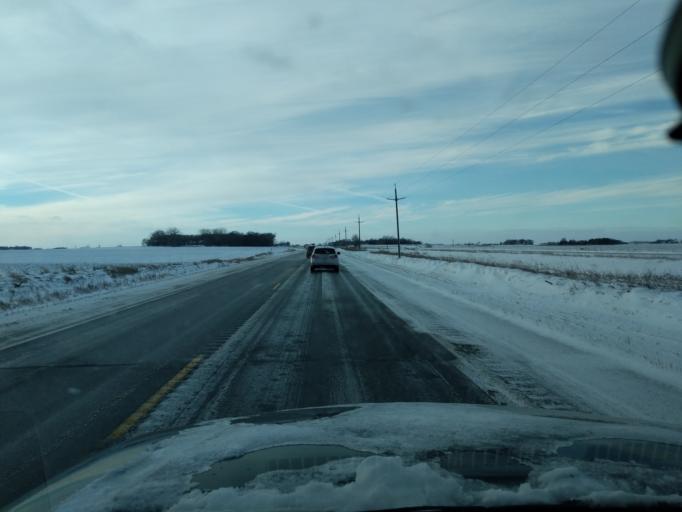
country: US
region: Minnesota
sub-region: Renville County
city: Hector
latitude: 44.7381
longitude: -94.6437
